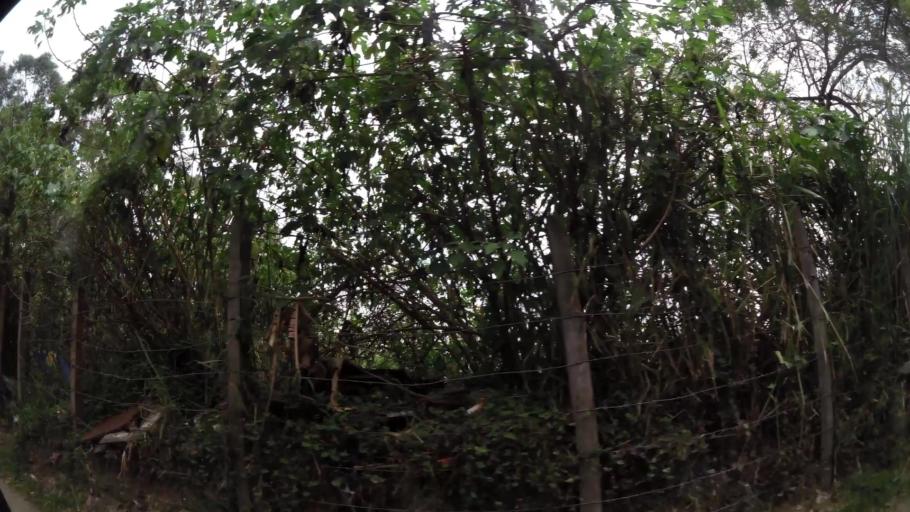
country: CO
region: Antioquia
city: Itagui
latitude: 6.2019
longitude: -75.5940
